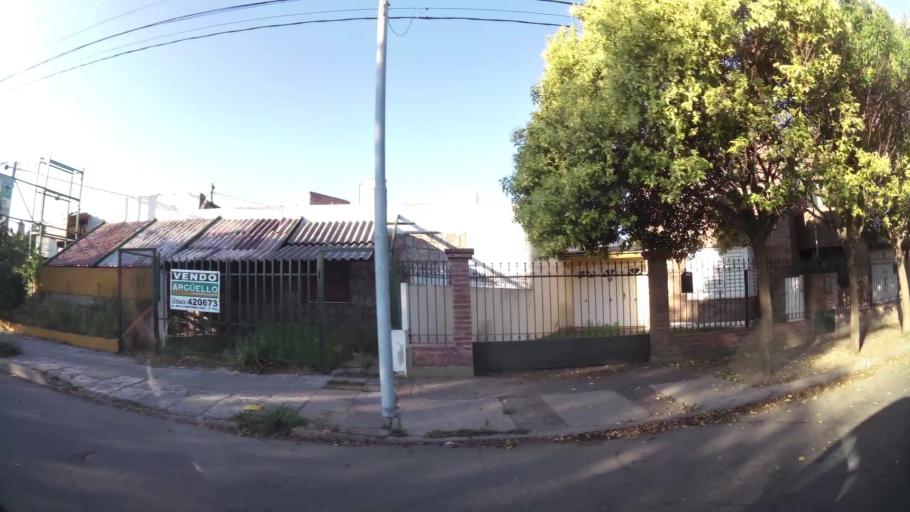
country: AR
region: Cordoba
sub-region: Departamento de Capital
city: Cordoba
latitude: -31.3707
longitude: -64.2052
